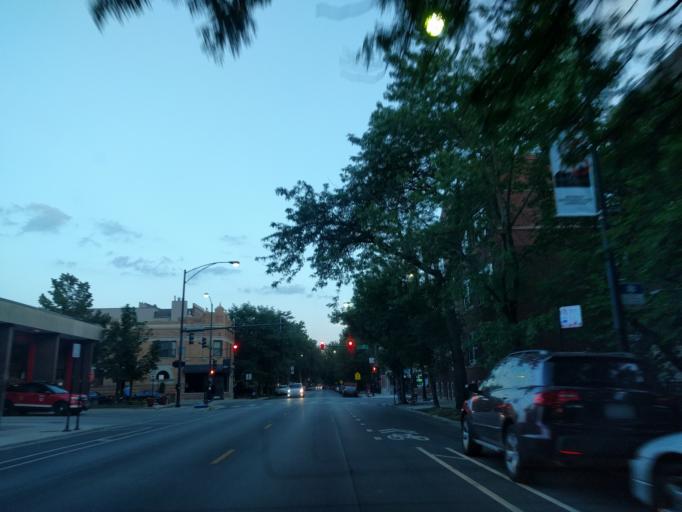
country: US
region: Illinois
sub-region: Cook County
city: Lincolnwood
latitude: 41.9510
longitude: -87.6787
